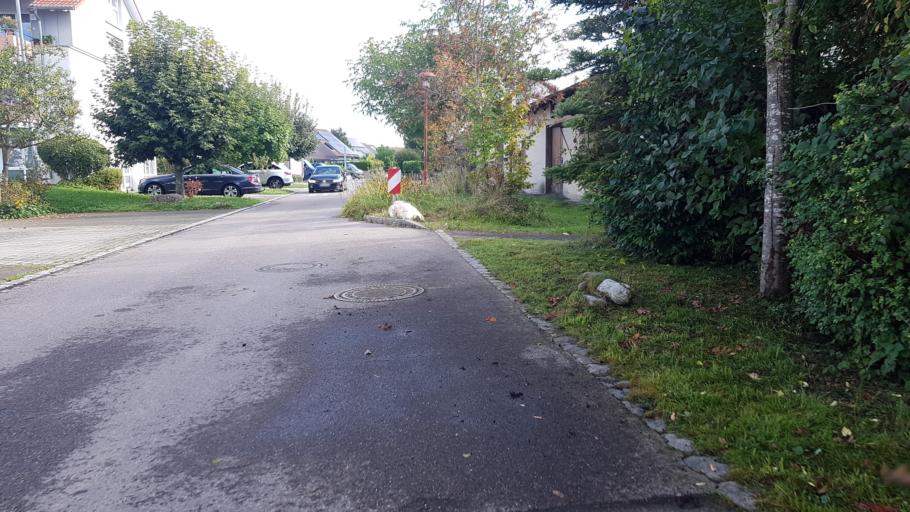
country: DE
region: Baden-Wuerttemberg
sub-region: Tuebingen Region
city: Langenargen
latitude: 47.6064
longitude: 9.5313
